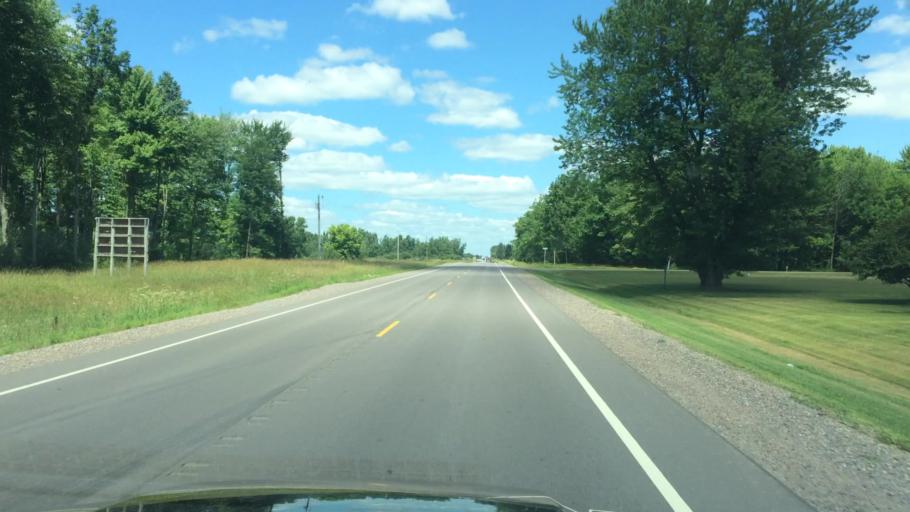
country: US
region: Wisconsin
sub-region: Clark County
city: Abbotsford
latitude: 45.0242
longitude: -90.3151
